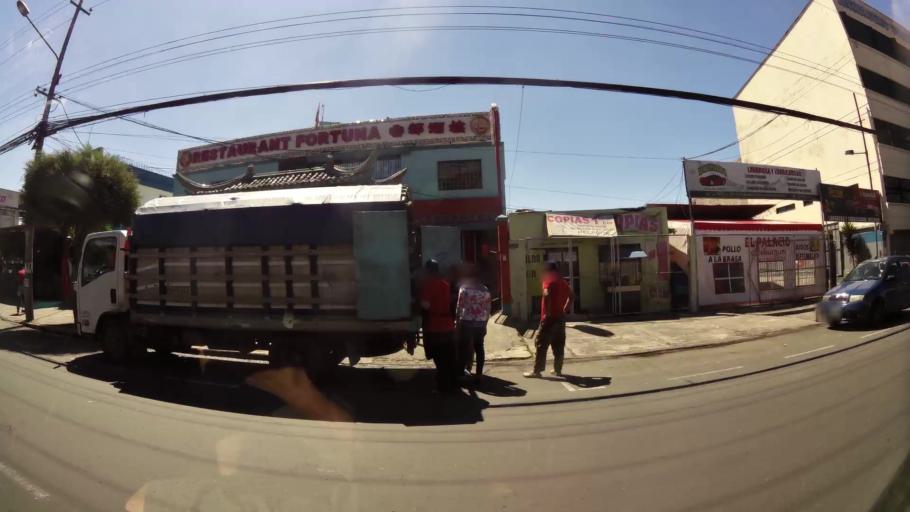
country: EC
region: Pichincha
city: Quito
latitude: -0.1553
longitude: -78.4886
